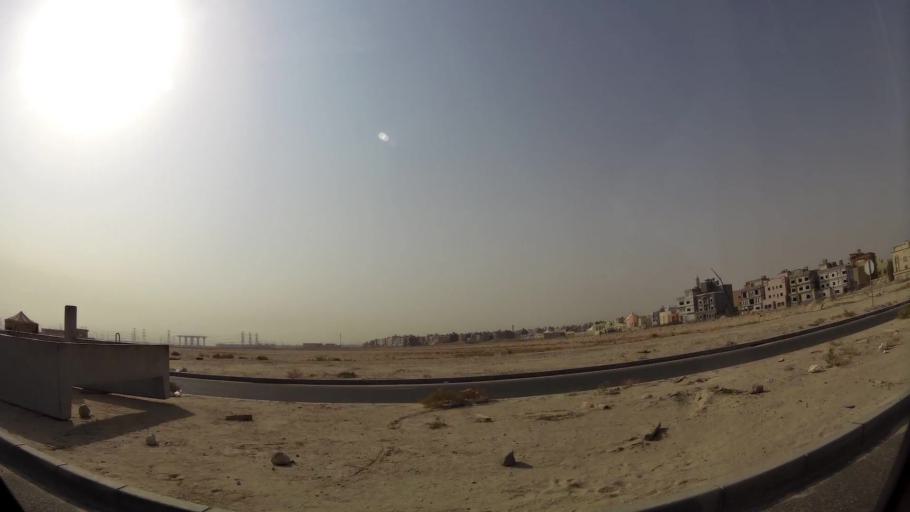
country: KW
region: Muhafazat al Jahra'
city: Al Jahra'
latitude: 29.3590
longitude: 47.7776
